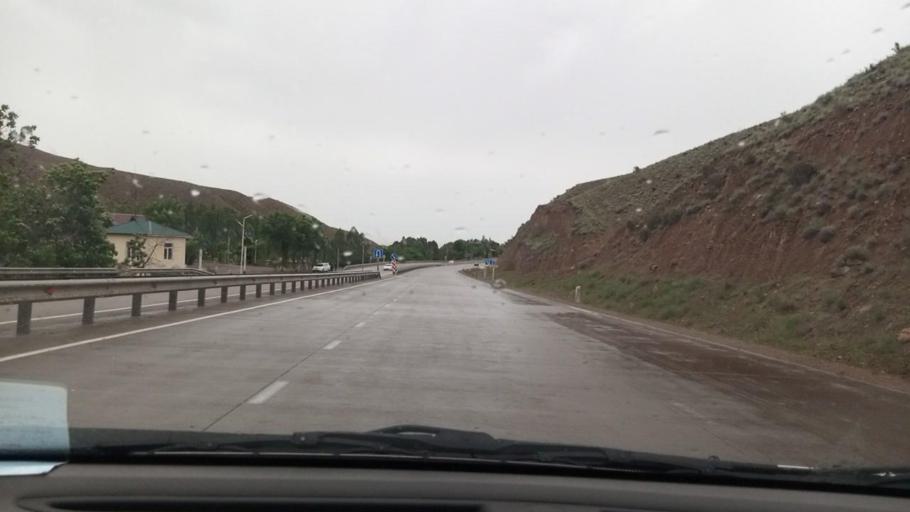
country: UZ
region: Namangan
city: Pop Shahri
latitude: 40.9508
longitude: 70.6777
